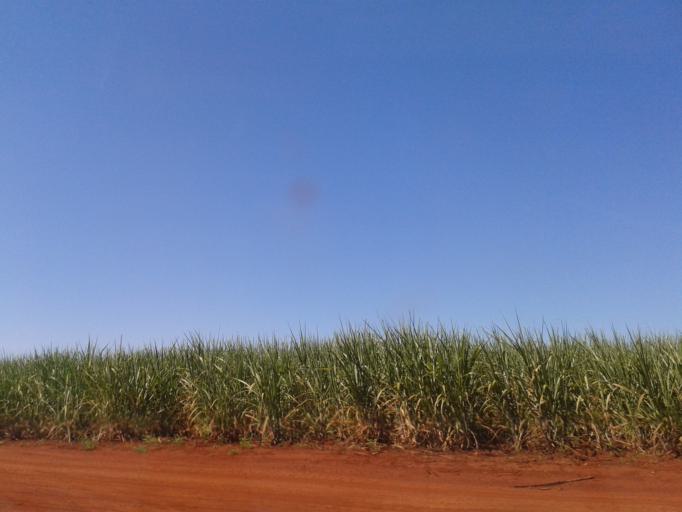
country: BR
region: Minas Gerais
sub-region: Centralina
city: Centralina
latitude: -18.6459
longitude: -49.2430
